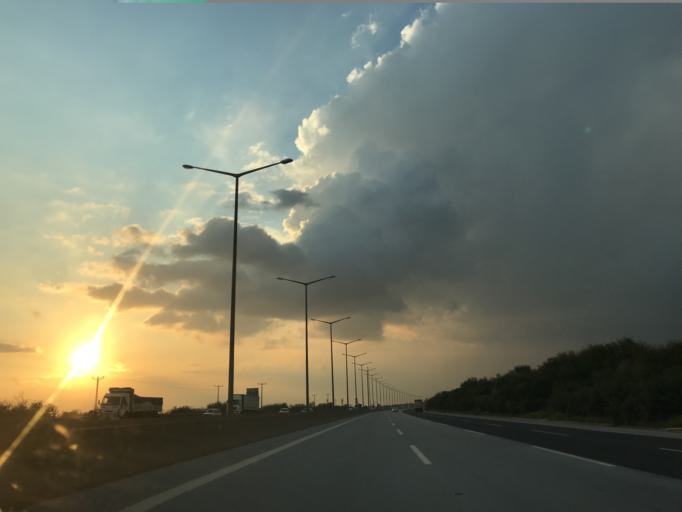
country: TR
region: Adana
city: Seyhan
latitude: 37.0305
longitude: 35.1962
